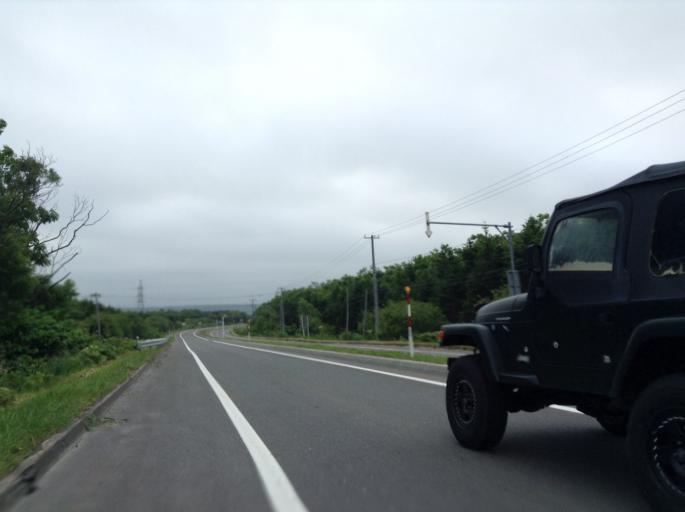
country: JP
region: Hokkaido
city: Wakkanai
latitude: 45.3704
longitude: 141.7237
